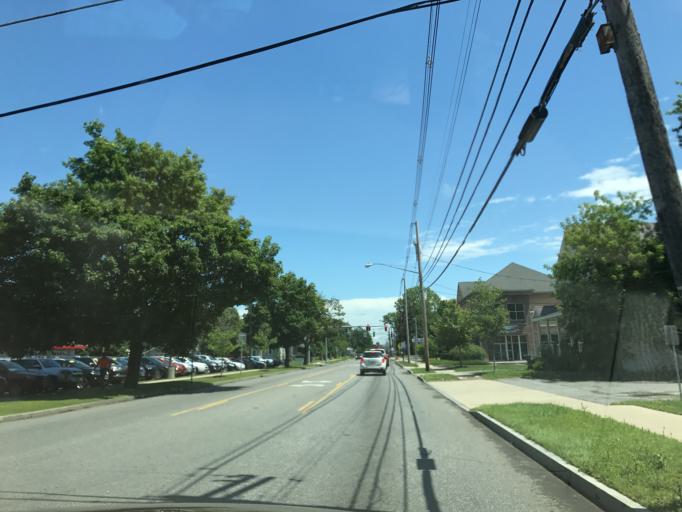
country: US
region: New York
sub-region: Warren County
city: Glens Falls
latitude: 43.3037
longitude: -73.6597
